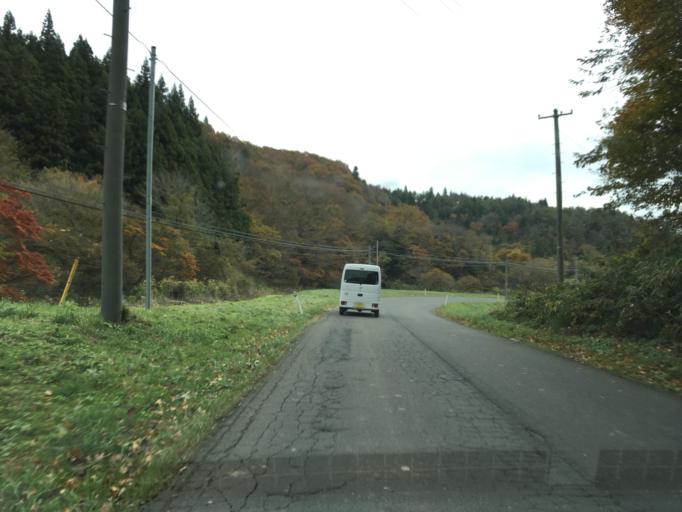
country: JP
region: Iwate
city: Mizusawa
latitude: 39.0882
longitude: 141.3487
